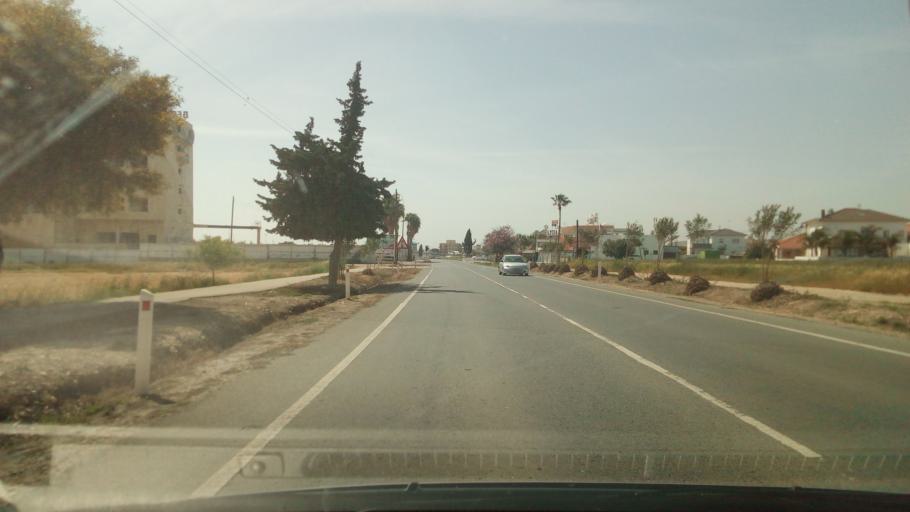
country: CY
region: Larnaka
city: Voroklini
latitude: 34.9776
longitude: 33.6873
